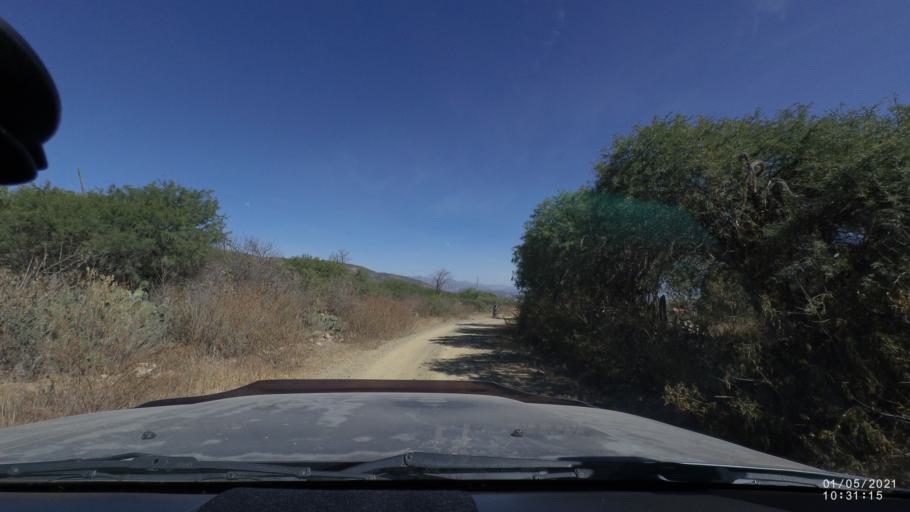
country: BO
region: Cochabamba
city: Capinota
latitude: -17.5931
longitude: -66.1943
